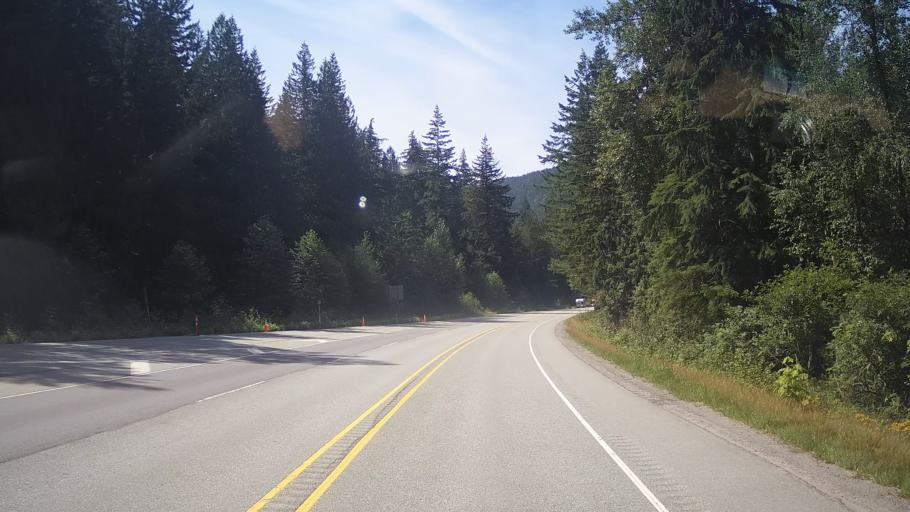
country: CA
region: British Columbia
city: Whistler
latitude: 49.9508
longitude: -123.1630
